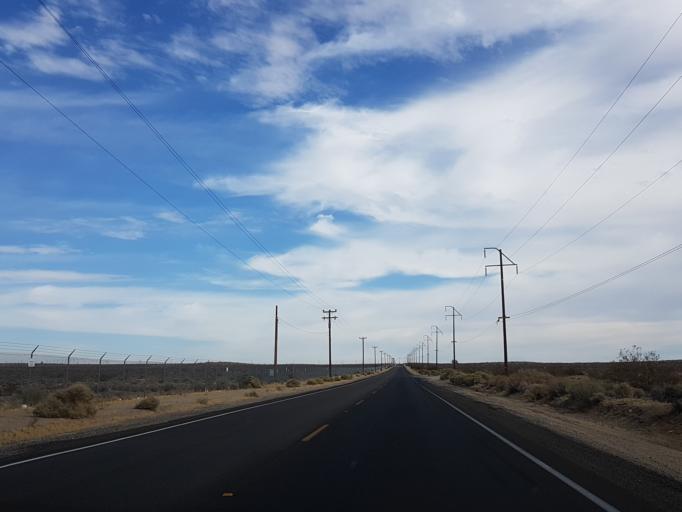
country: US
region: California
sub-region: Kern County
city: Ridgecrest
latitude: 35.6226
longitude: -117.6182
